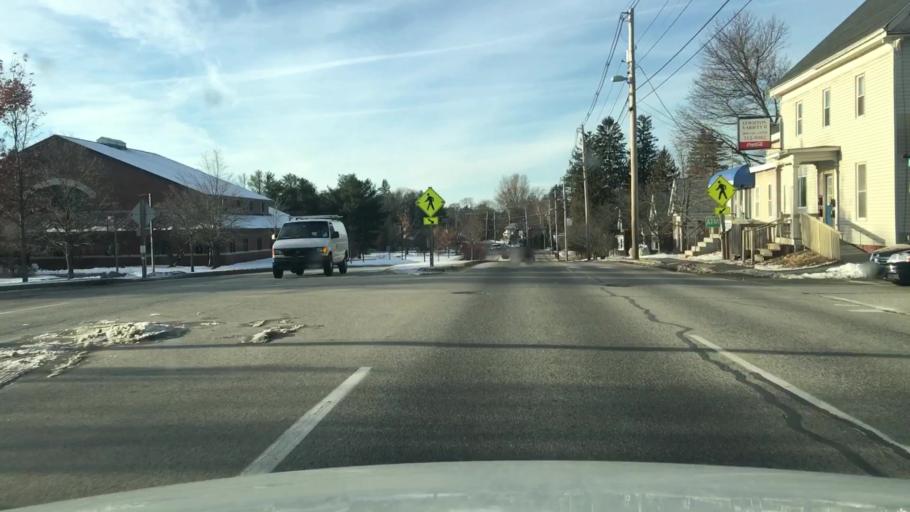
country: US
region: Maine
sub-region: Androscoggin County
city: Lewiston
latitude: 44.1081
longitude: -70.2006
